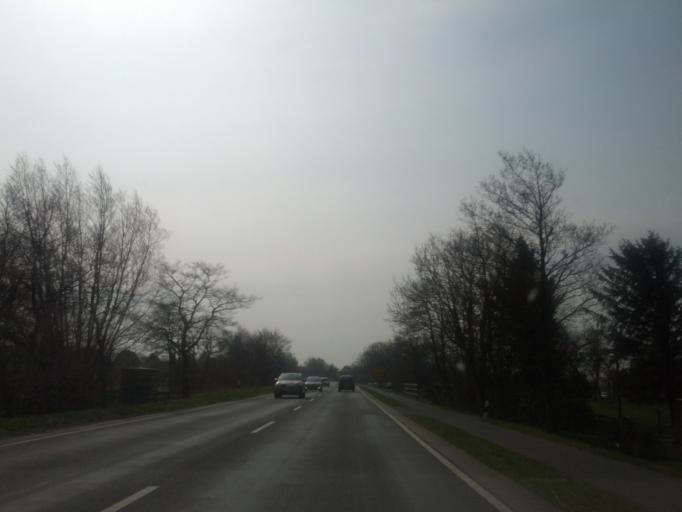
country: DE
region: Lower Saxony
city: Osteel
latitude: 53.5506
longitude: 7.2548
